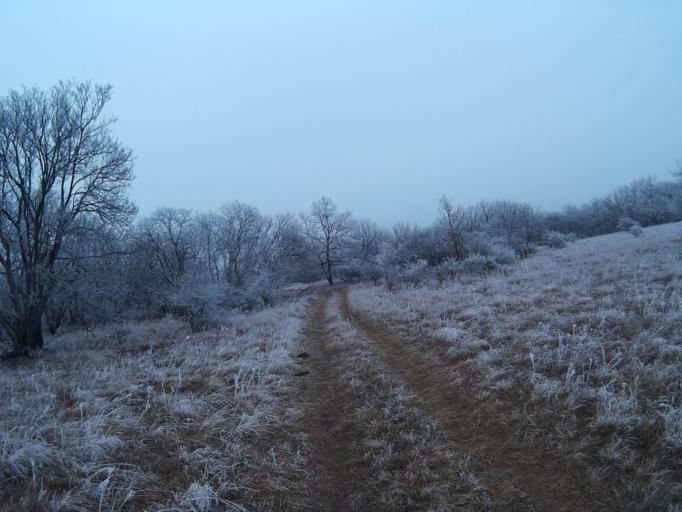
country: HU
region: Fejer
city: Csakvar
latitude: 47.3911
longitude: 18.4073
